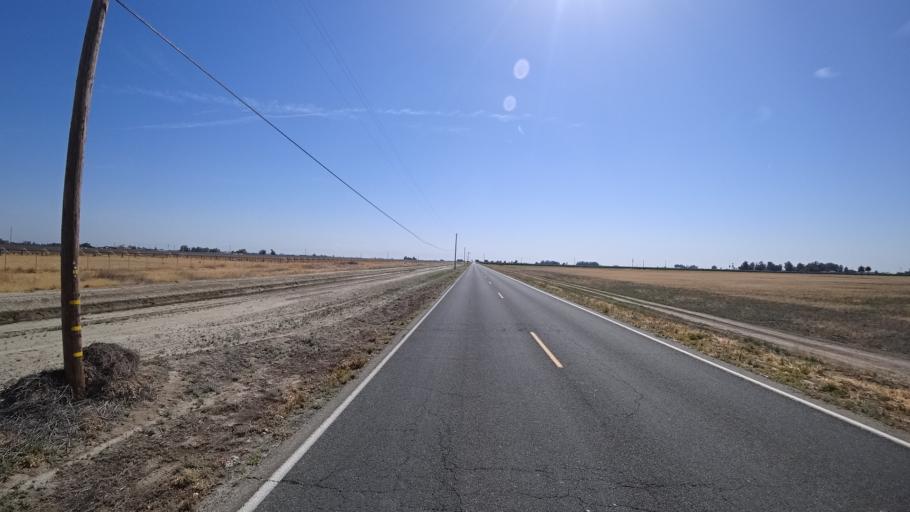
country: US
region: California
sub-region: Kings County
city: Stratford
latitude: 36.2115
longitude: -119.8024
